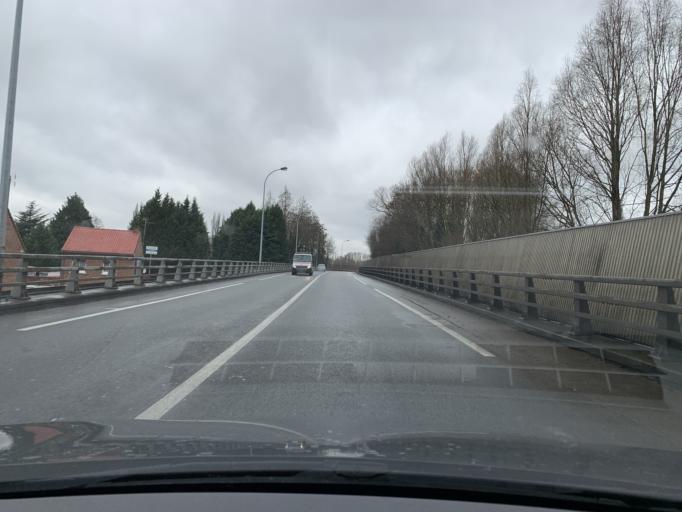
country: FR
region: Nord-Pas-de-Calais
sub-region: Departement du Nord
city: Sin-le-Noble
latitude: 50.3640
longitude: 3.1237
